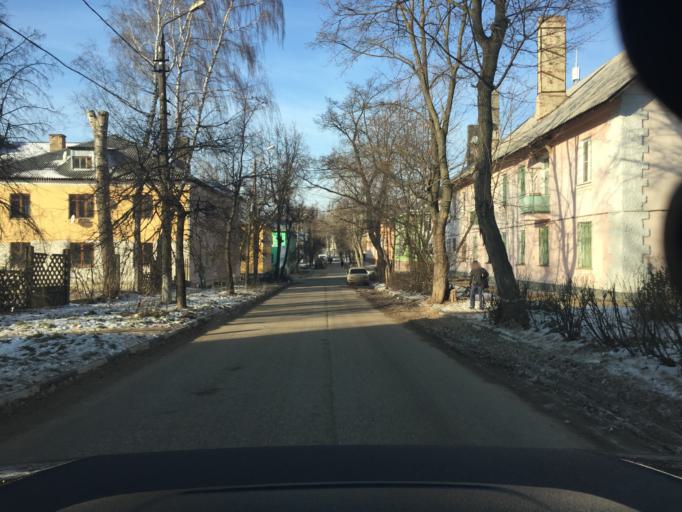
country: RU
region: Tula
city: Tula
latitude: 54.1821
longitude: 37.7054
